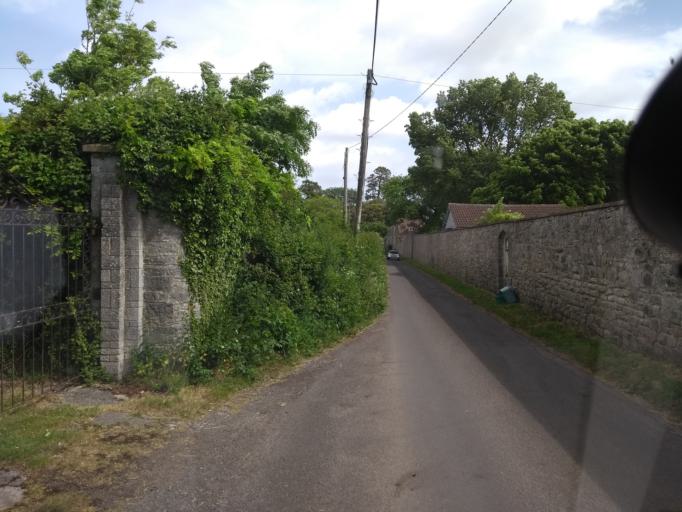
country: GB
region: England
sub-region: Somerset
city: Bridgwater
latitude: 51.1834
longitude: -3.0911
